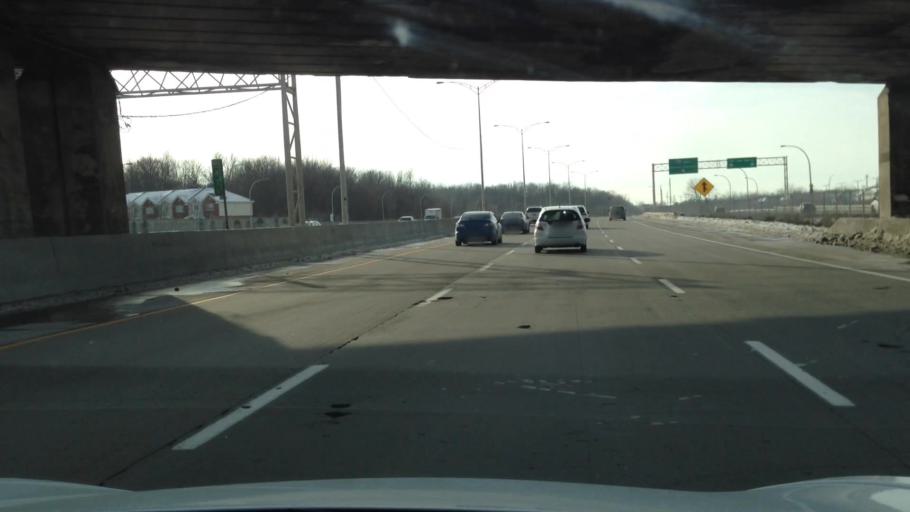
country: CA
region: Quebec
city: Beaconsfield
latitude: 45.4393
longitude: -73.8868
